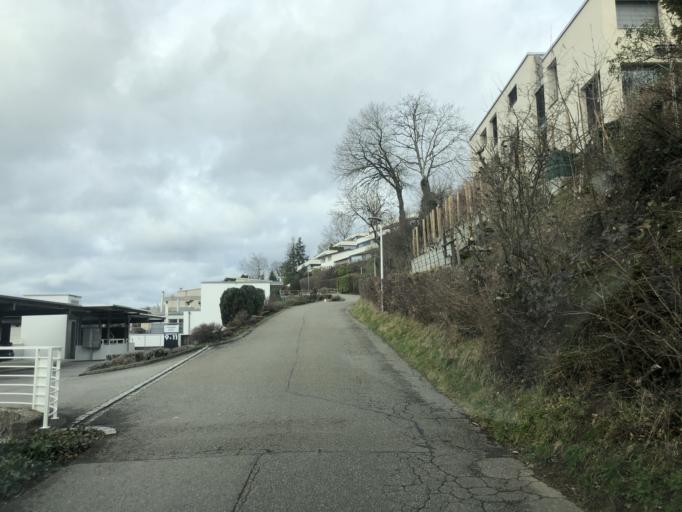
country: CH
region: Aargau
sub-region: Bezirk Baden
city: Obersiggenthal
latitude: 47.4907
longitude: 8.2951
